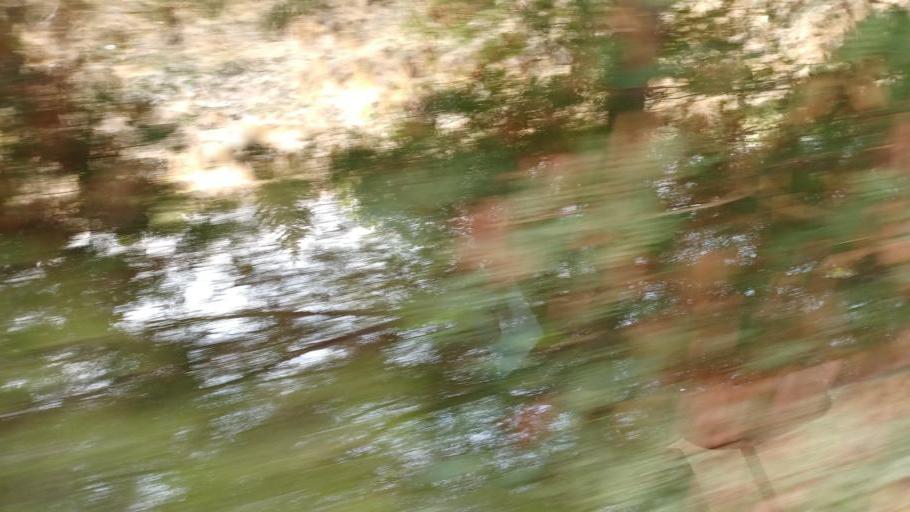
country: CY
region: Larnaka
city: Troulloi
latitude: 35.0078
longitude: 33.5706
